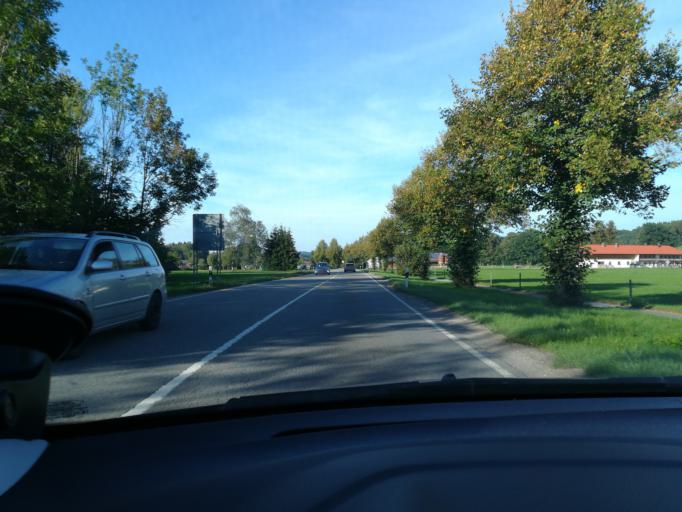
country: DE
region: Bavaria
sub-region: Upper Bavaria
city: Miesbach
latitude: 47.7726
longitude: 11.8271
